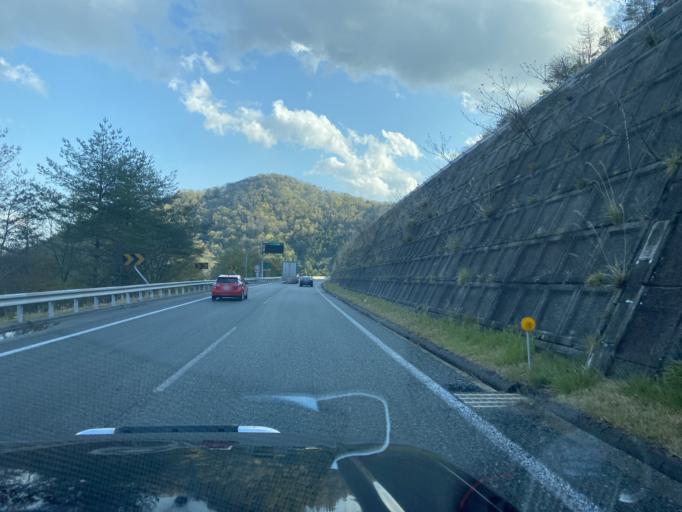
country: JP
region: Hyogo
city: Sasayama
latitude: 34.9851
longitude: 135.1514
